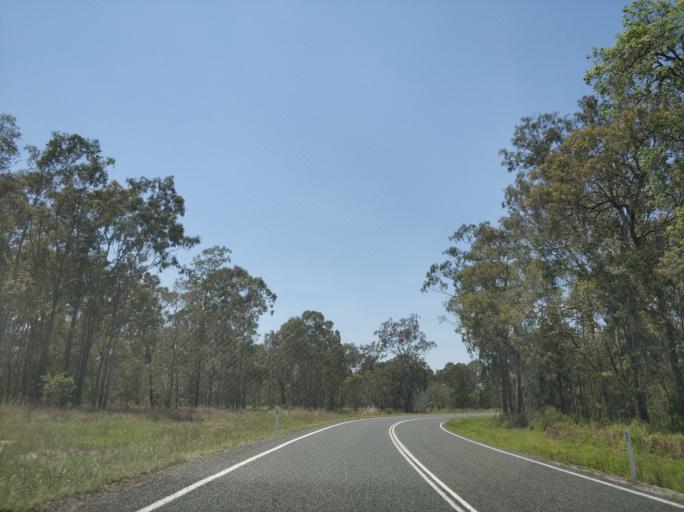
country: AU
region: Queensland
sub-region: Gladstone
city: Toolooa
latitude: -24.3255
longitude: 151.5745
